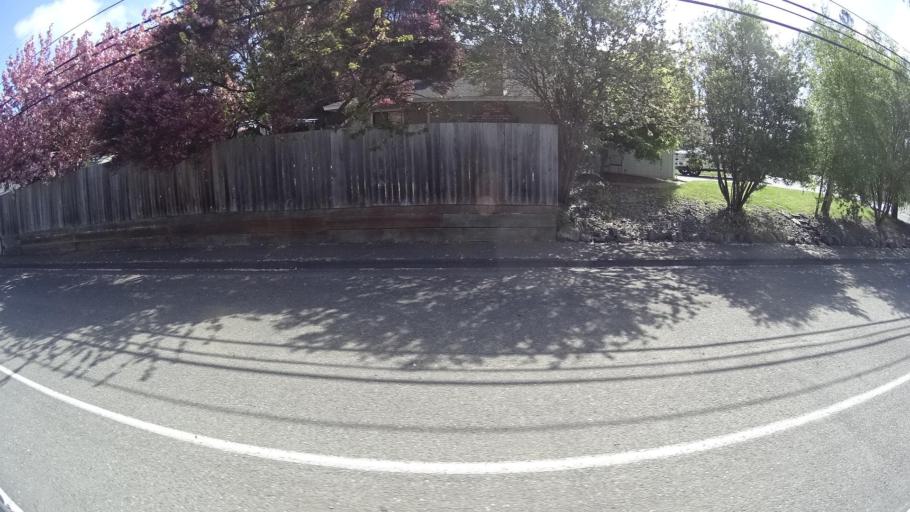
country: US
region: California
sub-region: Humboldt County
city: Pine Hills
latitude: 40.7417
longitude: -124.1474
